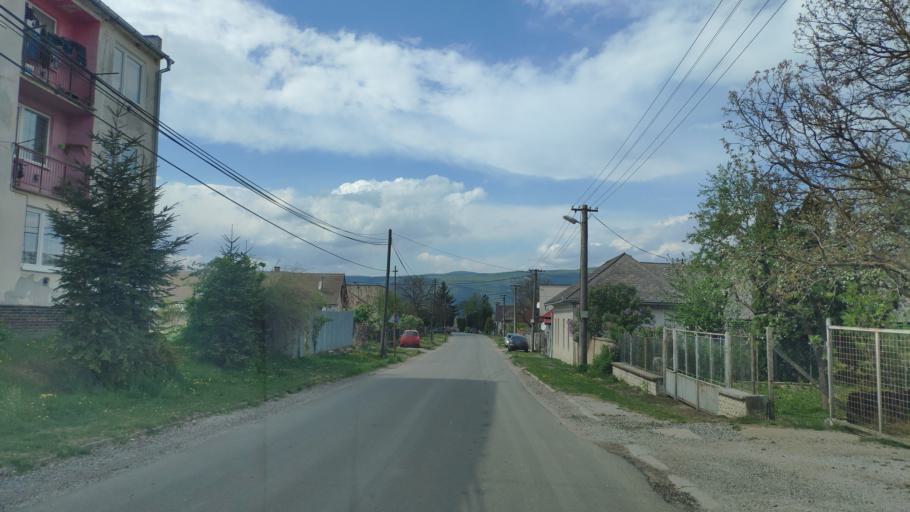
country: SK
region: Kosicky
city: Moldava nad Bodvou
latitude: 48.5825
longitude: 20.9224
